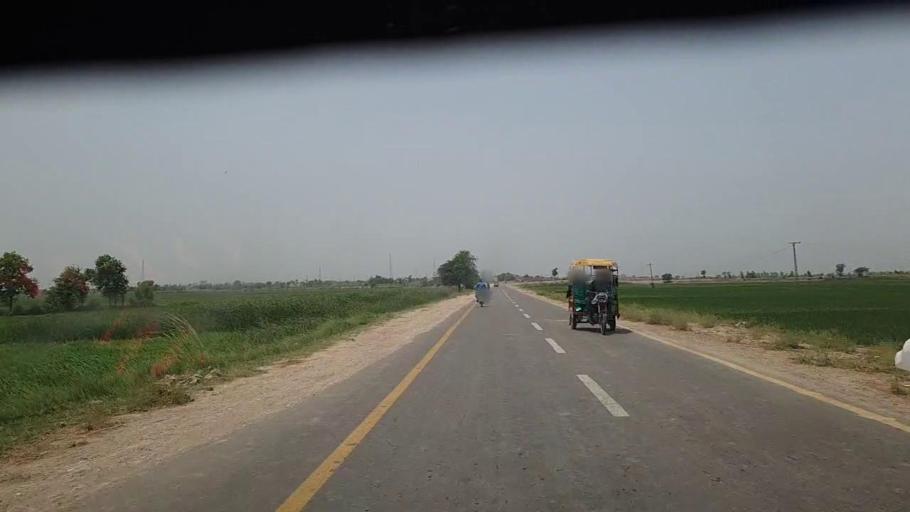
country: PK
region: Sindh
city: Sita Road
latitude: 27.0410
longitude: 67.8634
